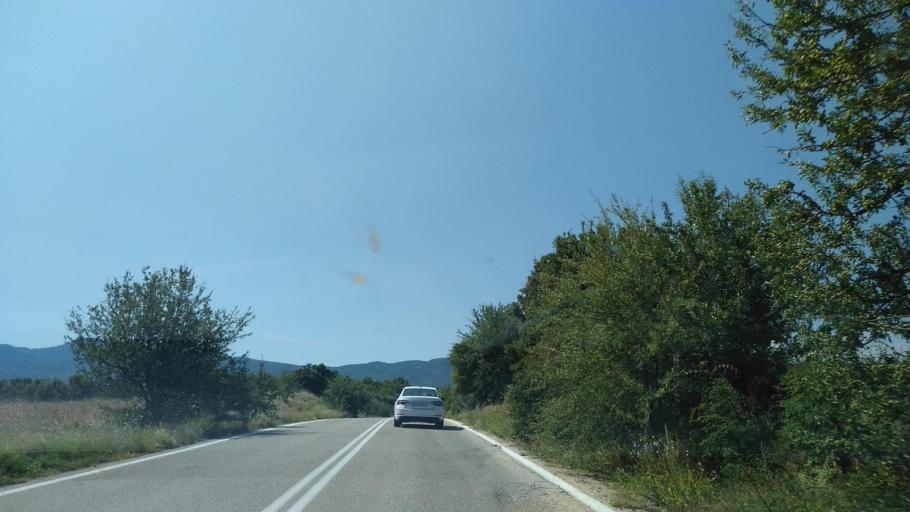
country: GR
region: Central Macedonia
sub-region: Nomos Thessalonikis
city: Nea Apollonia
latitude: 40.5386
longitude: 23.4691
